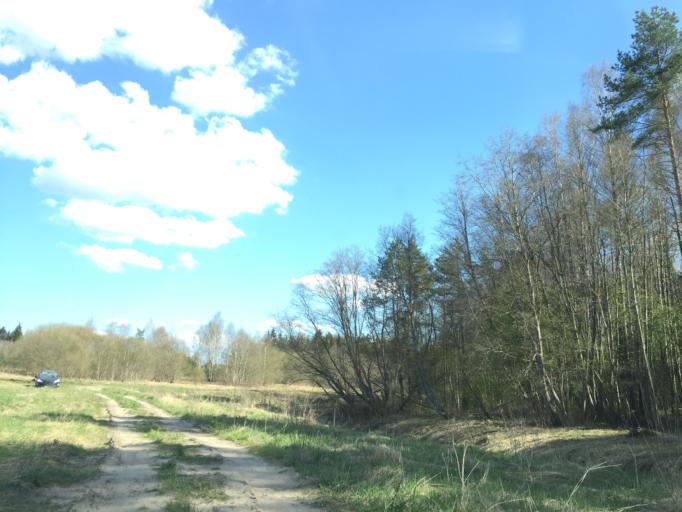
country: LV
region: Krimulda
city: Ragana
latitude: 57.3425
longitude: 24.6968
